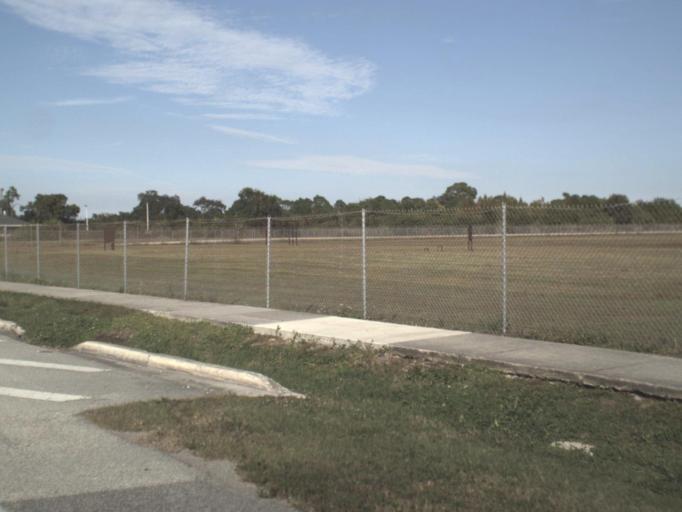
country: US
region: Florida
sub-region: Brevard County
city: June Park
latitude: 28.0627
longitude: -80.6707
